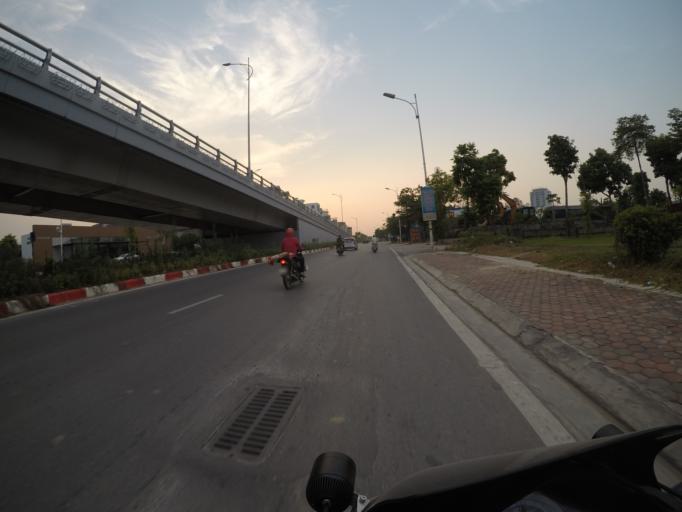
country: VN
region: Ha Noi
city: Trau Quy
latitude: 21.0275
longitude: 105.8958
